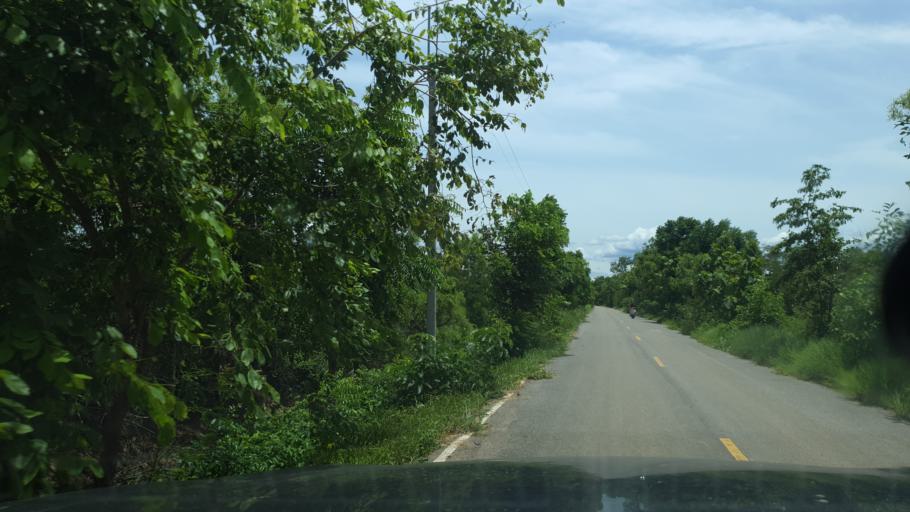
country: TH
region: Sukhothai
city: Ban Na
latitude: 17.1257
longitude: 99.6730
